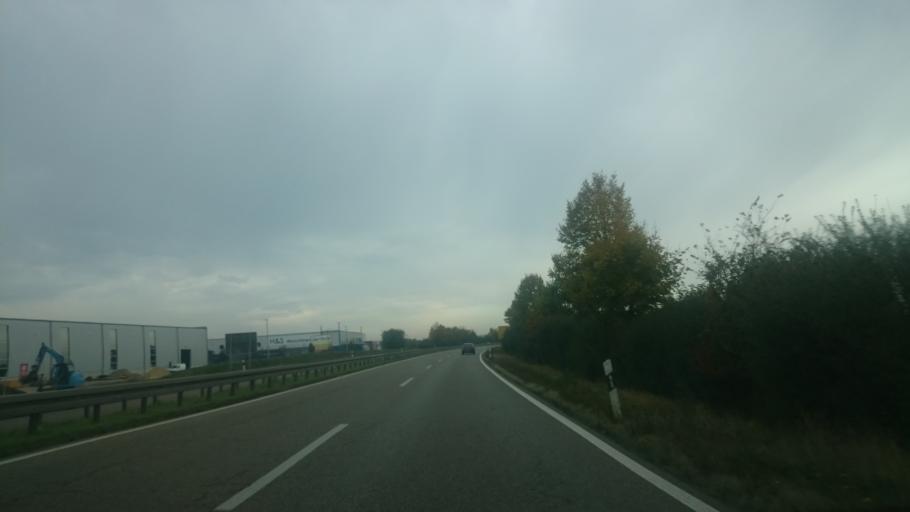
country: DE
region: Bavaria
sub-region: Swabia
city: Westendorf
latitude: 48.5651
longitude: 10.8480
